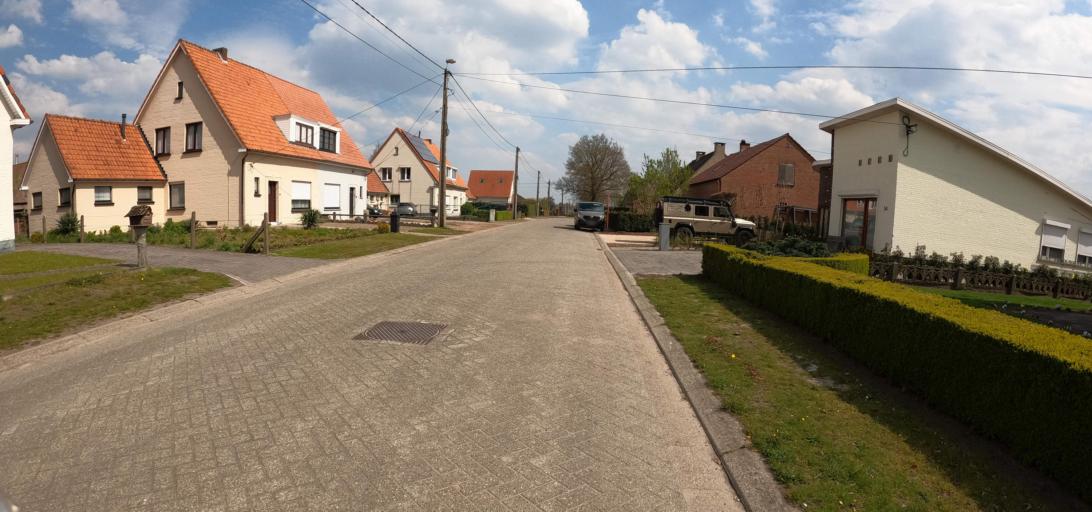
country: BE
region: Flanders
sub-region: Provincie Antwerpen
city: Oostmalle
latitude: 51.3001
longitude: 4.7488
